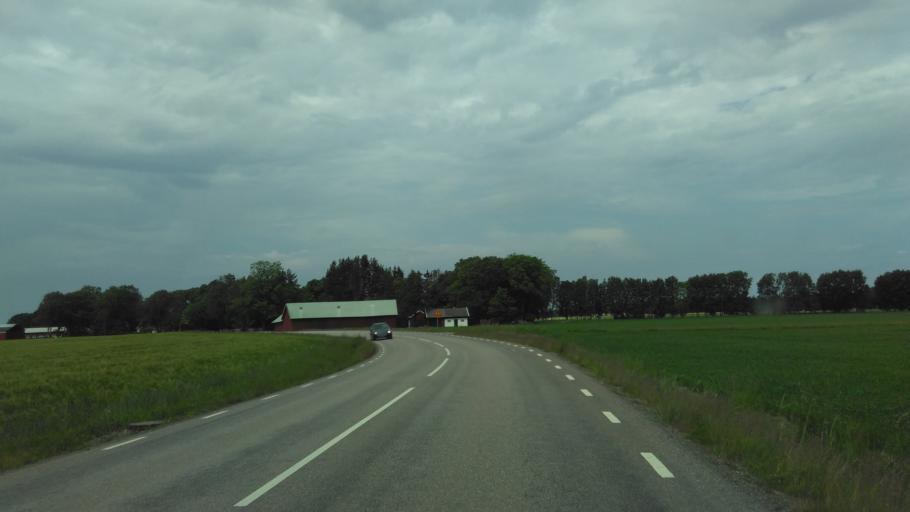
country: SE
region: Vaestra Goetaland
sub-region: Lidkopings Kommun
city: Lidkoping
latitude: 58.4647
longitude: 13.1497
